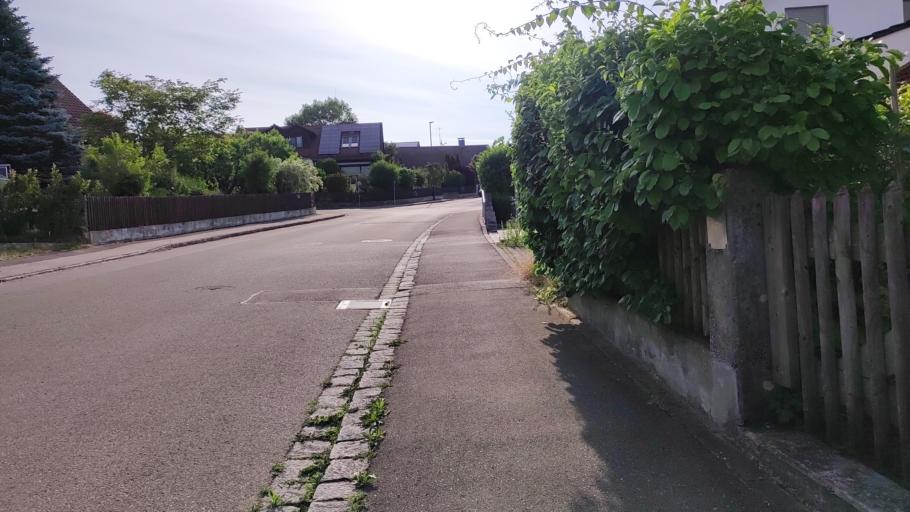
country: DE
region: Bavaria
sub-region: Swabia
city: Horgau
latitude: 48.3986
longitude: 10.6951
